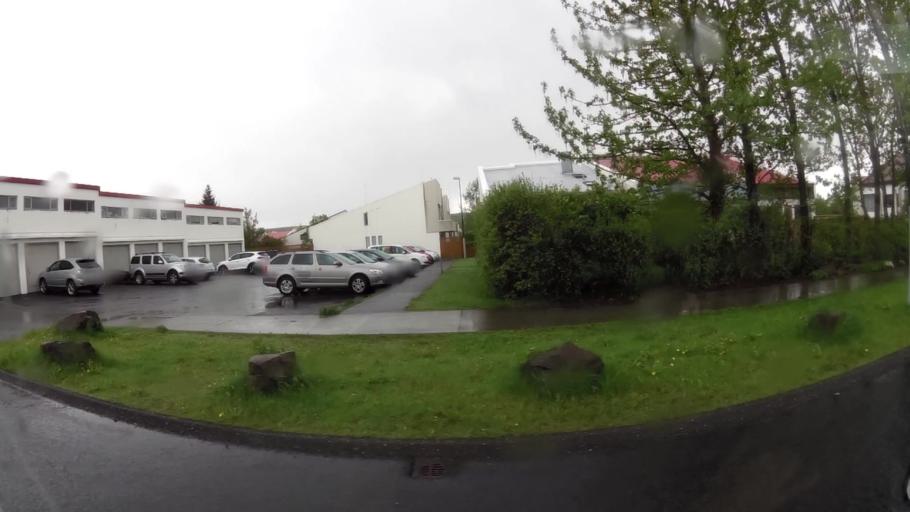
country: IS
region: Capital Region
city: Reykjavik
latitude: 64.0974
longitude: -21.8326
